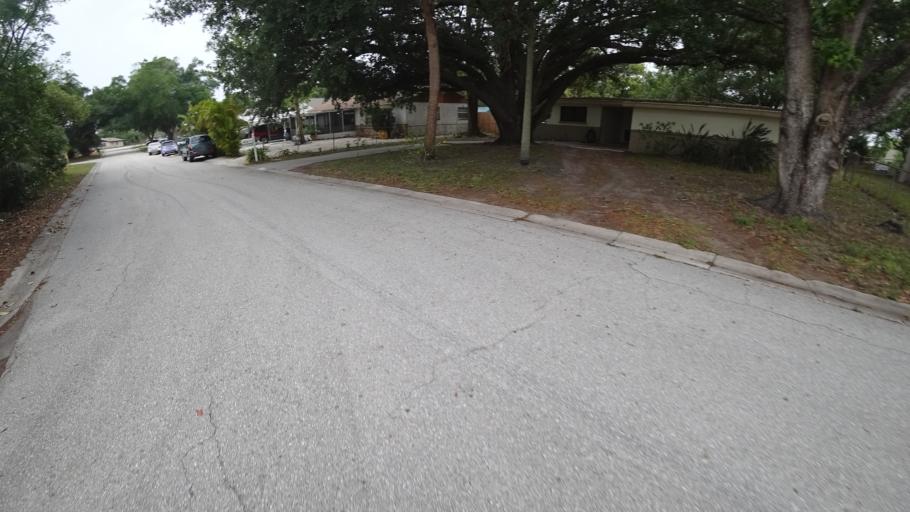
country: US
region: Florida
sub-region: Manatee County
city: Samoset
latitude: 27.4430
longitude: -82.5092
